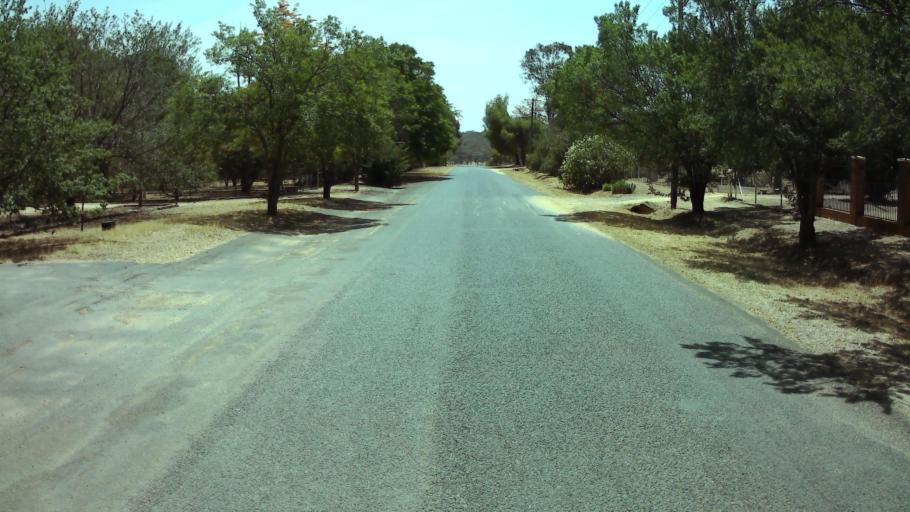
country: AU
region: New South Wales
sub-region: Weddin
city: Grenfell
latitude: -33.8959
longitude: 148.1721
